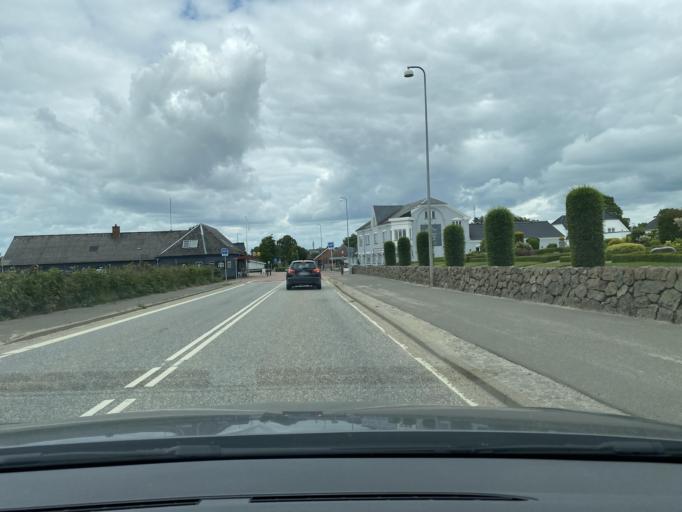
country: DK
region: South Denmark
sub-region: Vejle Kommune
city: Jelling
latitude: 55.6727
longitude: 9.4348
